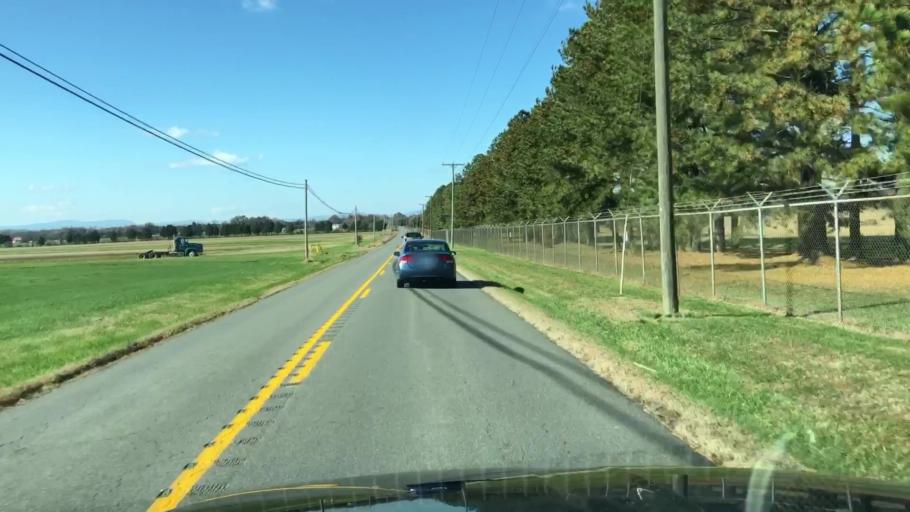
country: US
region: Virginia
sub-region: Fauquier County
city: Bealeton
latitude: 38.5155
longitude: -77.7869
